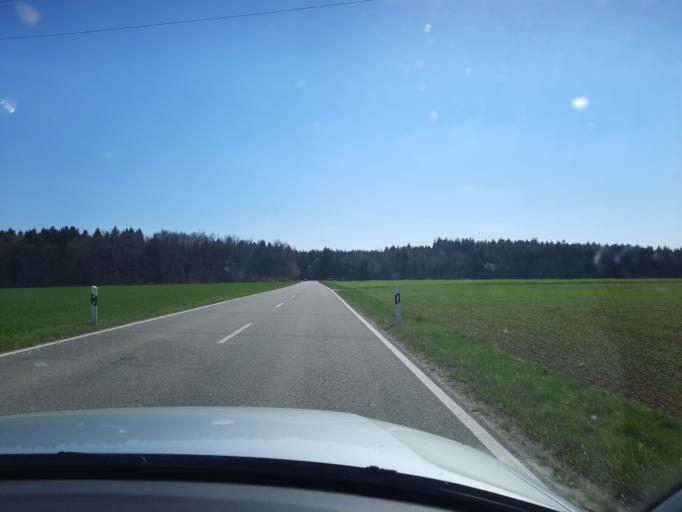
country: DE
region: Bavaria
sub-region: Upper Bavaria
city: Zorneding
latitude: 48.0707
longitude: 11.8222
